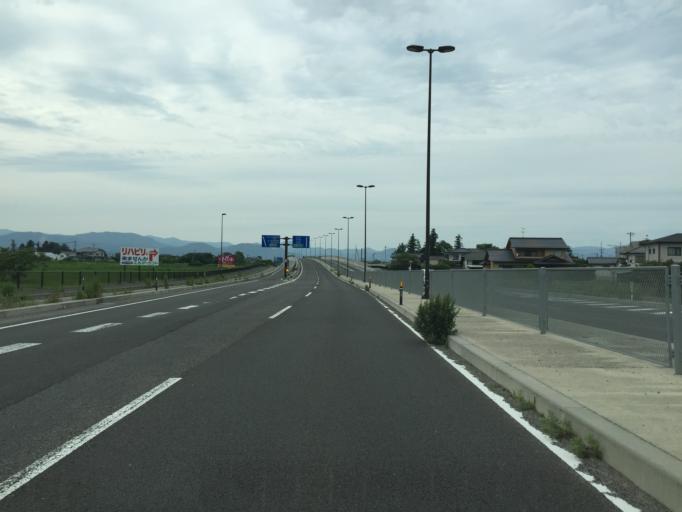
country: JP
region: Fukushima
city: Fukushima-shi
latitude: 37.7370
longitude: 140.4408
